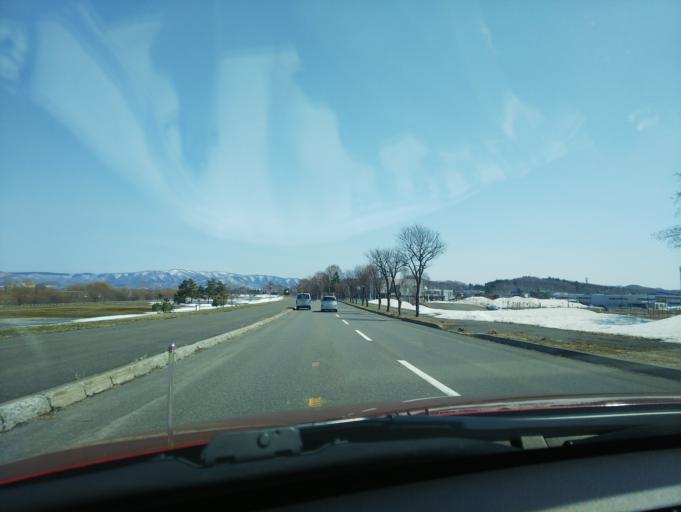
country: JP
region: Hokkaido
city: Nayoro
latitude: 44.1909
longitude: 142.3930
